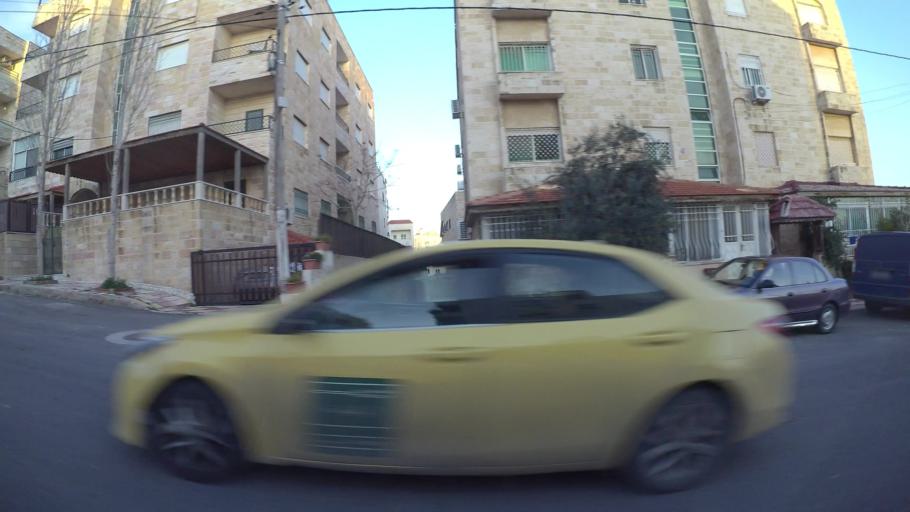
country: JO
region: Amman
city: Al Jubayhah
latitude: 31.9992
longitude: 35.8625
